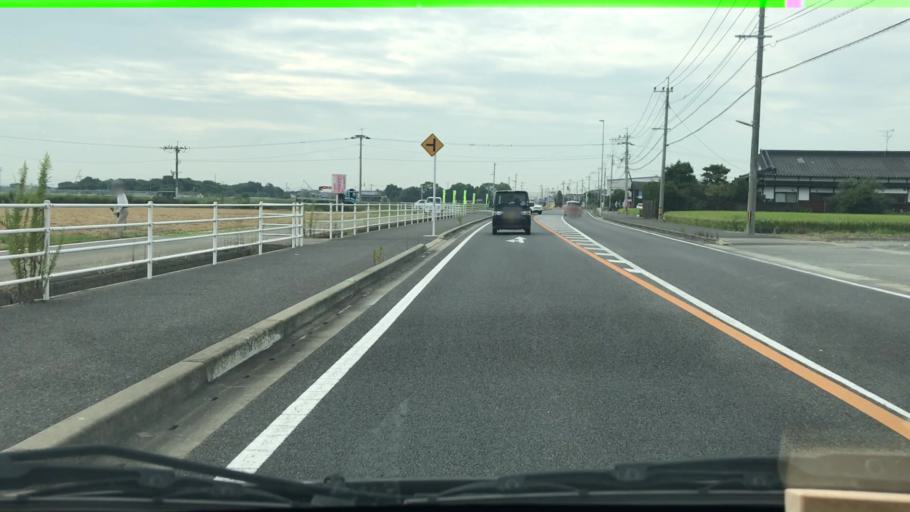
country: JP
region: Saga Prefecture
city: Saga-shi
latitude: 33.2284
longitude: 130.2576
